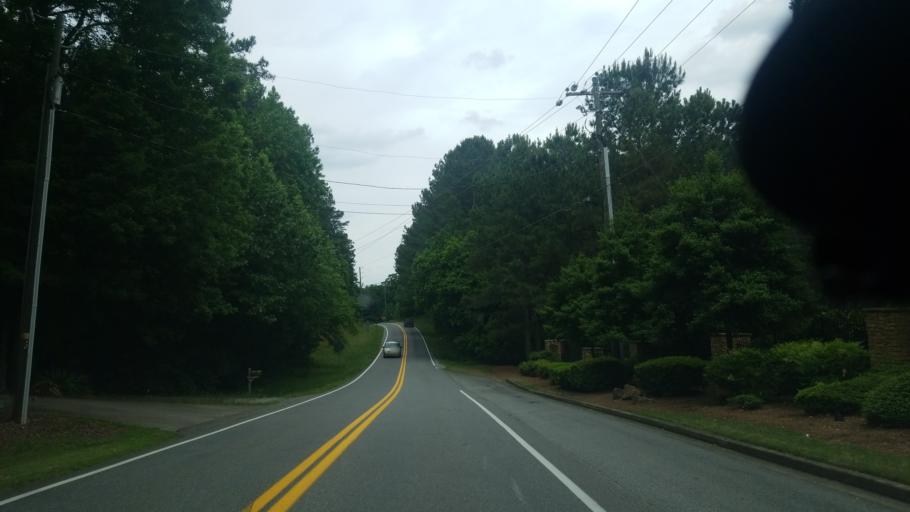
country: US
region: Georgia
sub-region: Forsyth County
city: Cumming
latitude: 34.1501
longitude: -84.1572
